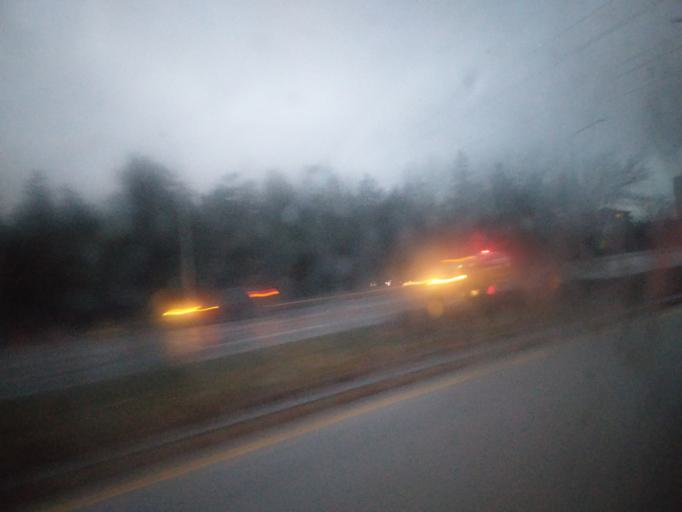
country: TR
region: Ankara
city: Ankara
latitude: 39.9540
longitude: 32.8207
